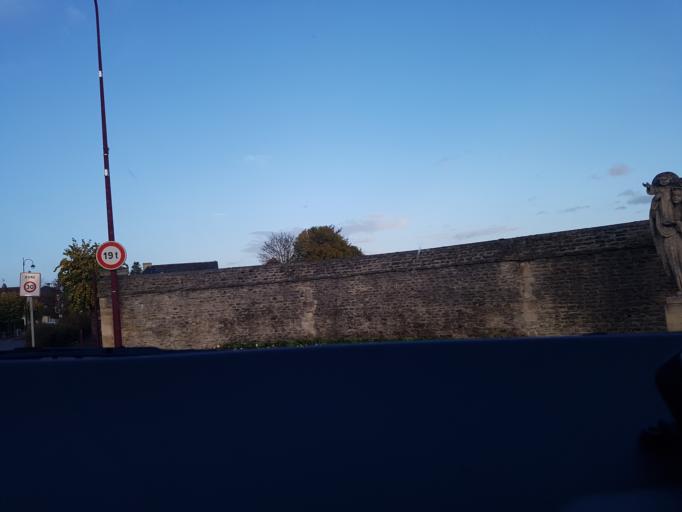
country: FR
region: Lower Normandy
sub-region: Departement du Calvados
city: Troarn
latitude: 49.1796
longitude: -0.1862
